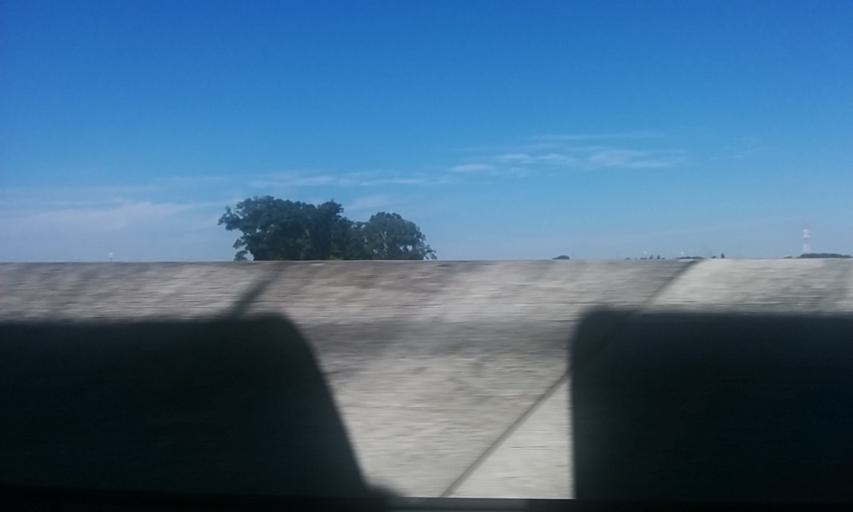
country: JP
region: Ibaraki
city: Moriya
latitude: 35.9176
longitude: 139.9595
